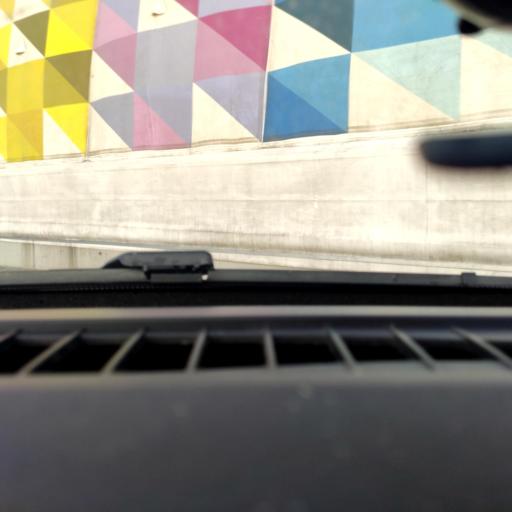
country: RU
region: Voronezj
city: Voronezh
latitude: 51.6727
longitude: 39.2373
